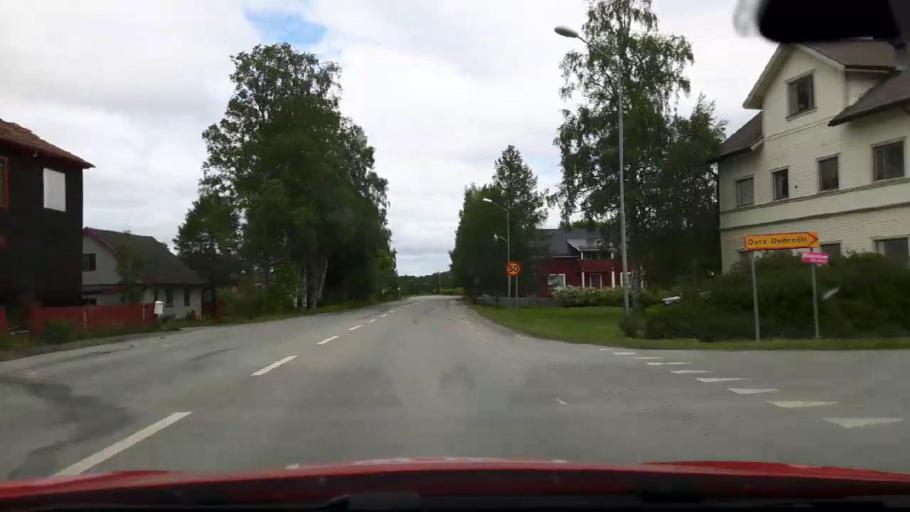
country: SE
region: Jaemtland
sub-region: Krokoms Kommun
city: Krokom
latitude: 63.3033
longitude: 14.4712
